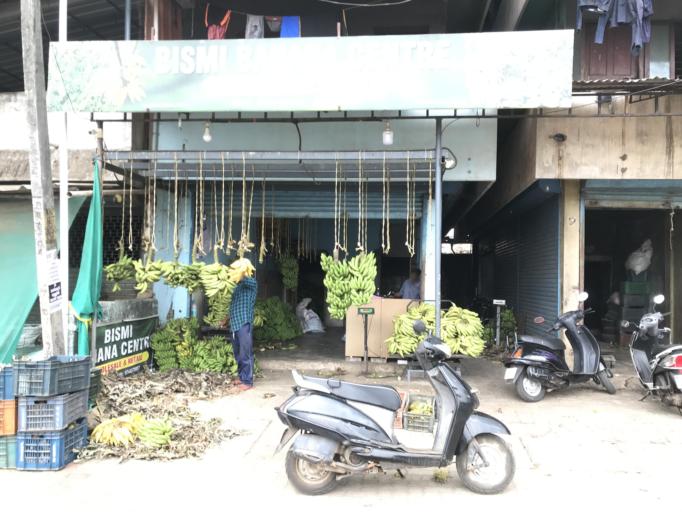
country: IN
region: Kerala
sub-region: Ernakulam
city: Aluva
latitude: 10.1064
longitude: 76.3493
